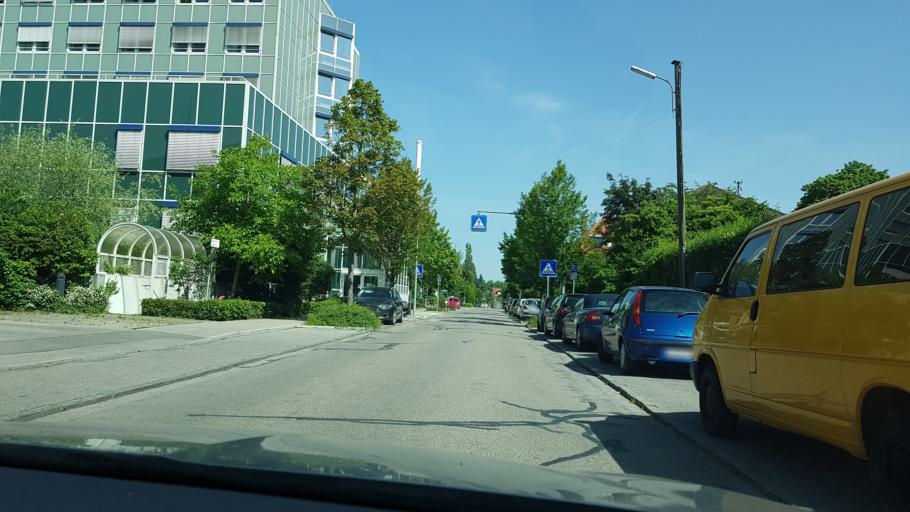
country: DE
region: Bavaria
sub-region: Upper Bavaria
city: Fuerstenfeldbruck
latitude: 48.1806
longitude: 11.2603
